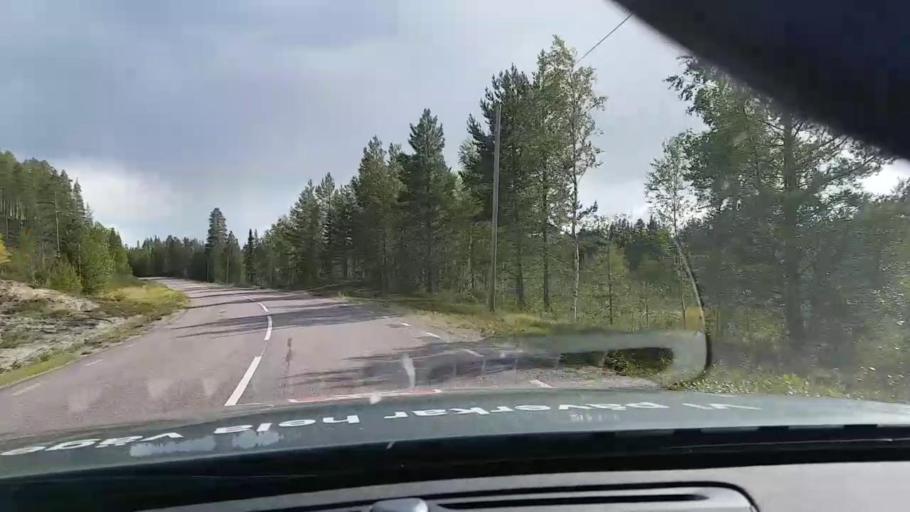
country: SE
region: Vaesterbotten
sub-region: Asele Kommun
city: Asele
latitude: 63.8681
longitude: 17.3593
